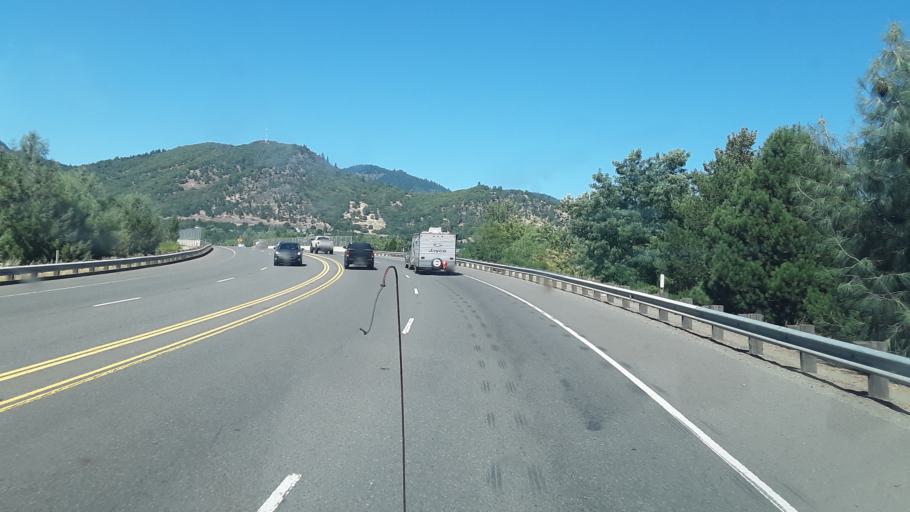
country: US
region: Oregon
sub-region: Josephine County
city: Fruitdale
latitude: 42.4333
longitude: -123.3132
